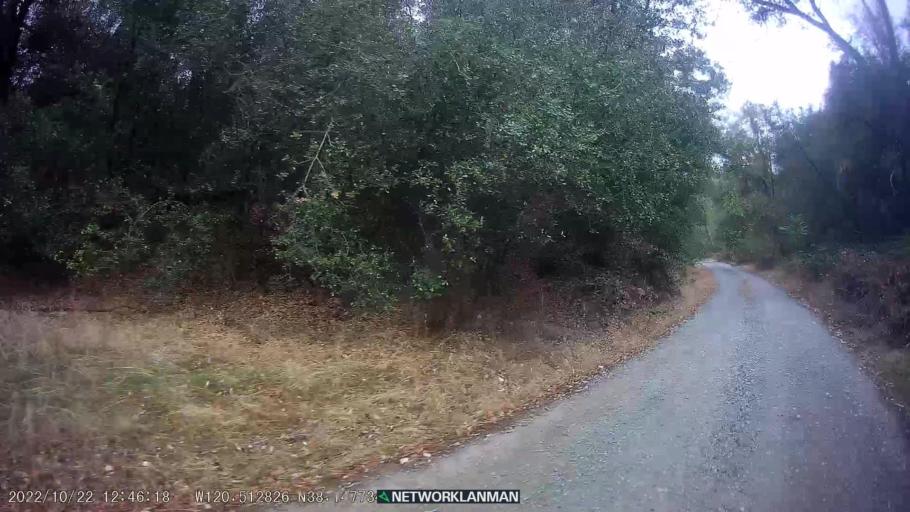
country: US
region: California
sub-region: Calaveras County
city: Murphys
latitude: 38.1478
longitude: -120.5127
